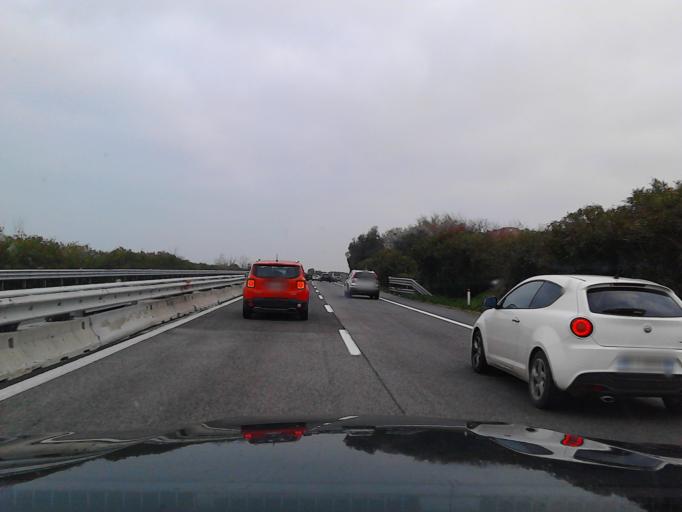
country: IT
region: Abruzzo
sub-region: Provincia di Teramo
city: Tortoreto Lido
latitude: 42.7963
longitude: 13.9313
